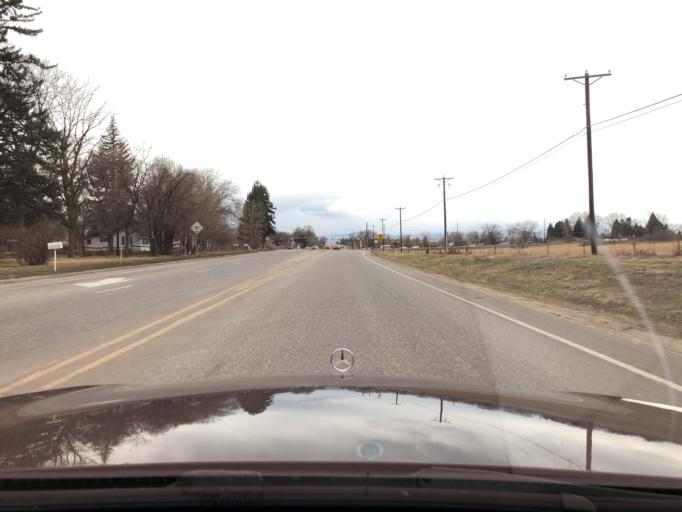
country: US
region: Colorado
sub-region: Boulder County
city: Gunbarrel
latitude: 40.0147
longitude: -105.1741
